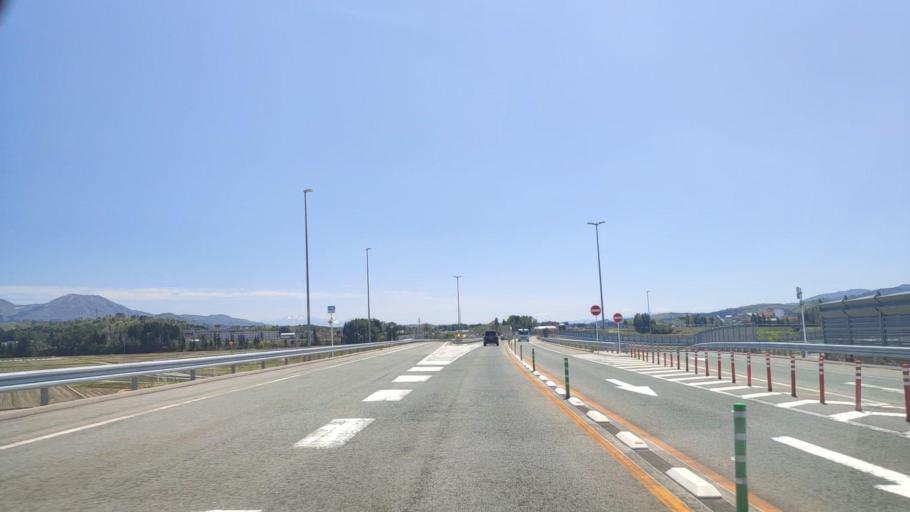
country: JP
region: Yamagata
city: Obanazawa
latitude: 38.6072
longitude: 140.3883
